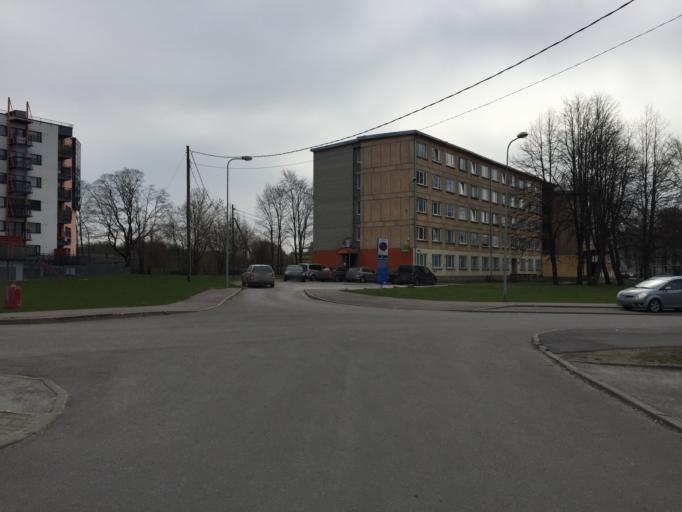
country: EE
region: Harju
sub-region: Tallinna linn
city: Tallinn
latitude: 59.4242
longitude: 24.7264
